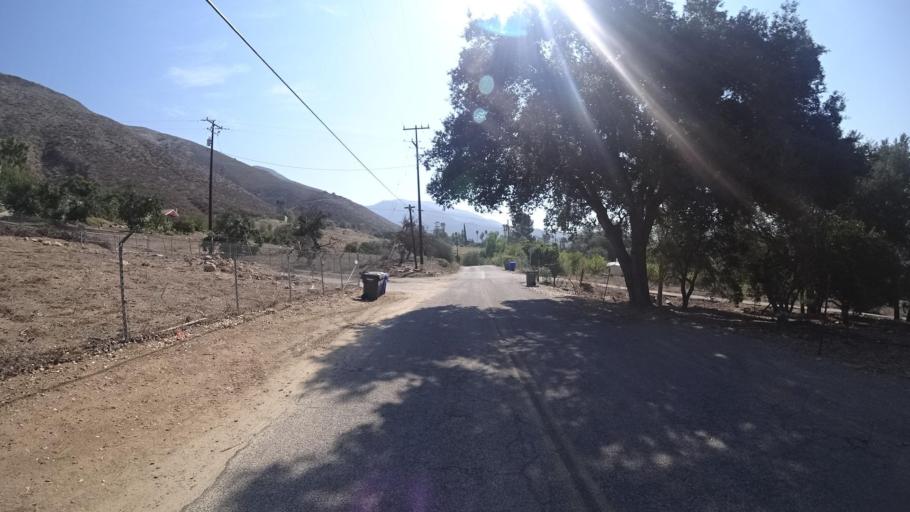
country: US
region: California
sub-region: San Diego County
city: Valley Center
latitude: 33.3416
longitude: -116.9946
